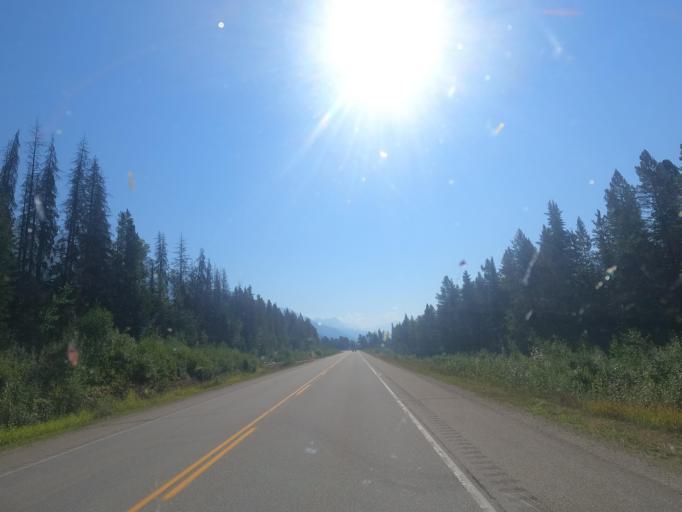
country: CA
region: Alberta
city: Jasper Park Lodge
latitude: 52.9750
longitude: -118.9597
